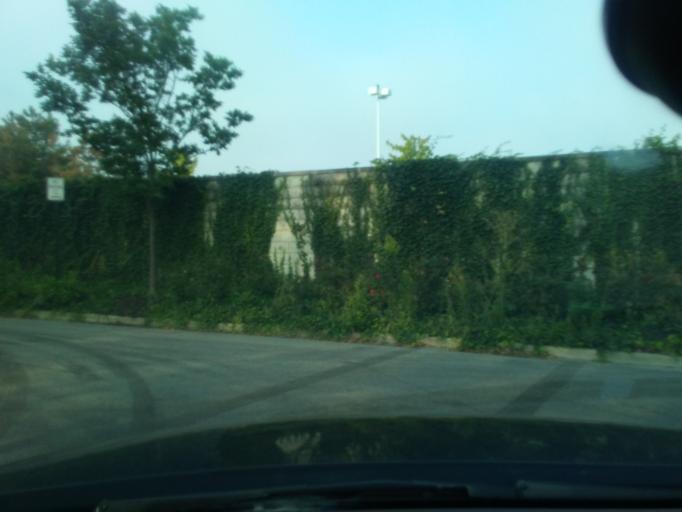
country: US
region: Illinois
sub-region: Cook County
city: Evanston
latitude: 42.0202
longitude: -87.7043
